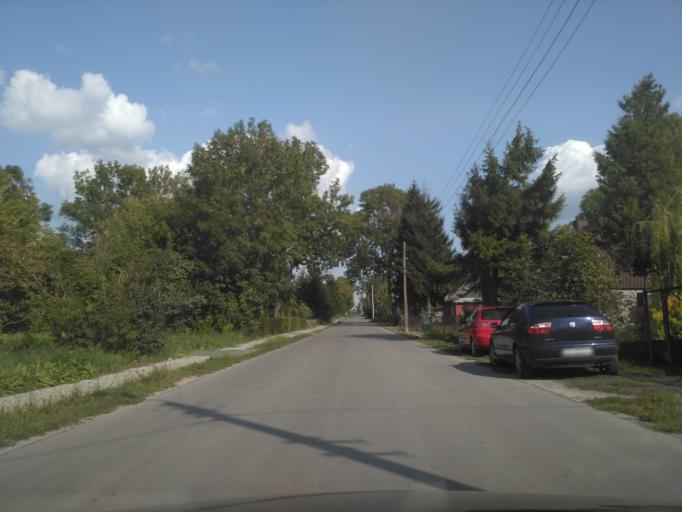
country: PL
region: Lublin Voivodeship
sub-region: Powiat chelmski
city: Pokrowka
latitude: 51.0689
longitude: 23.5099
